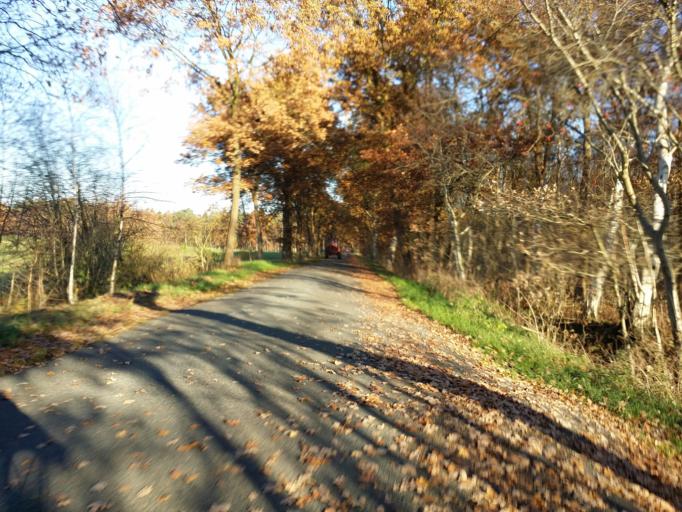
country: DE
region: Lower Saxony
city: Langwedel
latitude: 53.0273
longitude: 9.1817
